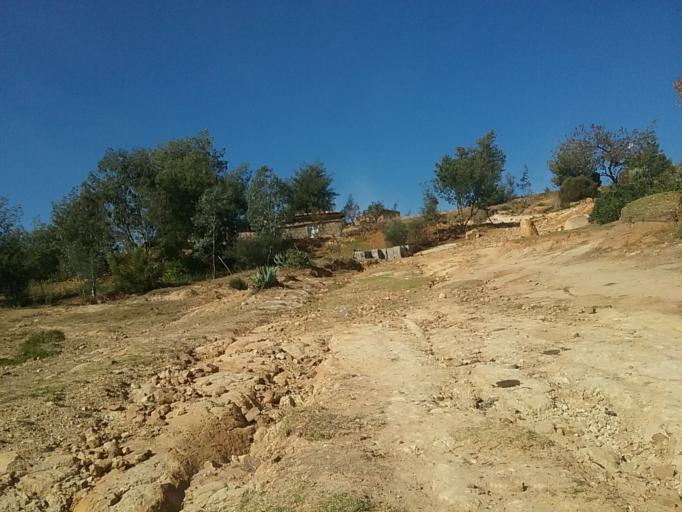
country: LS
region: Berea
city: Teyateyaneng
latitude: -29.2489
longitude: 27.9284
